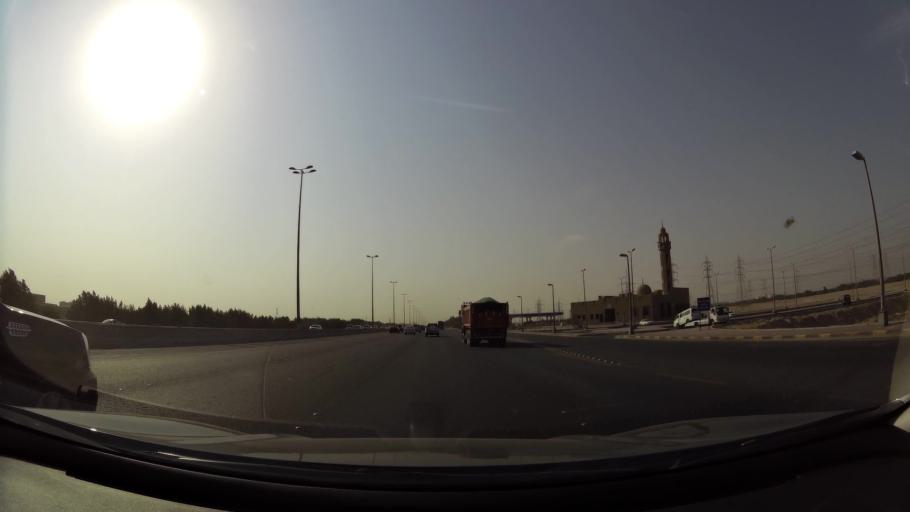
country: KW
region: Al Ahmadi
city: Ar Riqqah
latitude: 29.1166
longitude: 48.0940
